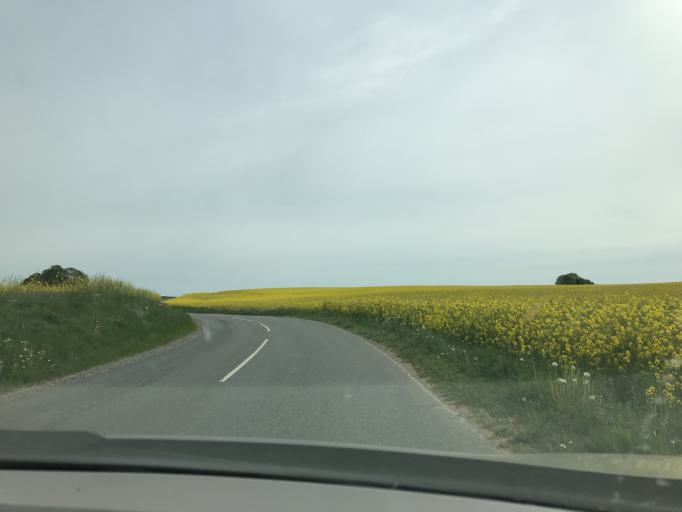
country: DK
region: Central Jutland
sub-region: Norddjurs Kommune
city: Allingabro
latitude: 56.5713
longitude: 10.2968
